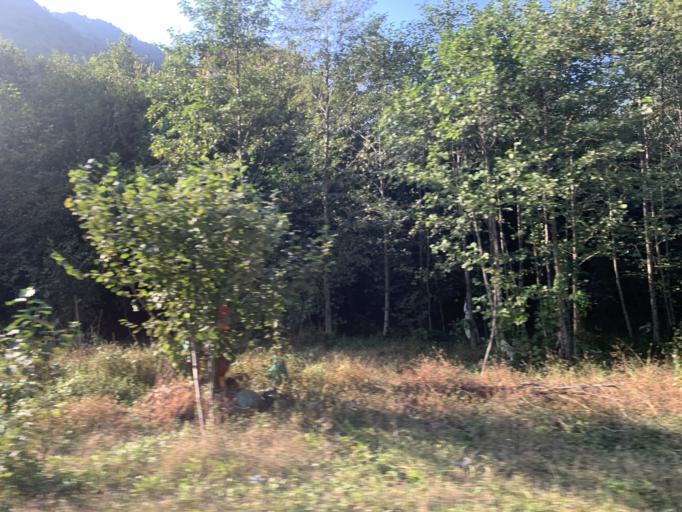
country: TR
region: Trabzon
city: Dernekpazari
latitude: 40.8476
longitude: 40.2814
